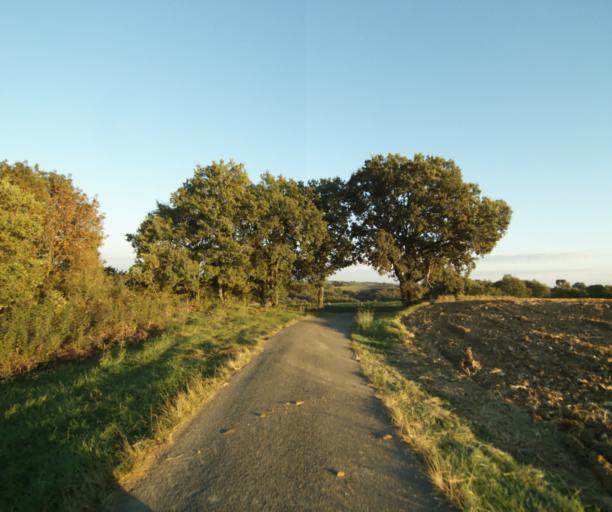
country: FR
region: Midi-Pyrenees
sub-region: Departement du Gers
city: Vic-Fezensac
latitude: 43.7490
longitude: 0.1893
